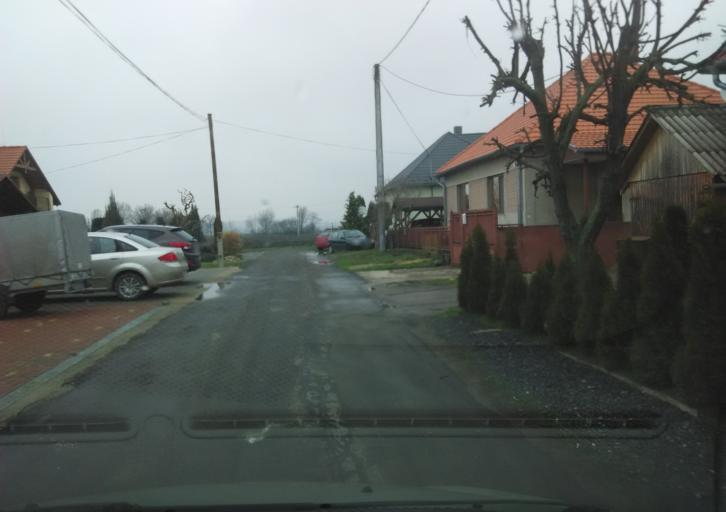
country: SK
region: Nitriansky
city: Tlmace
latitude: 48.2754
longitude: 18.5420
